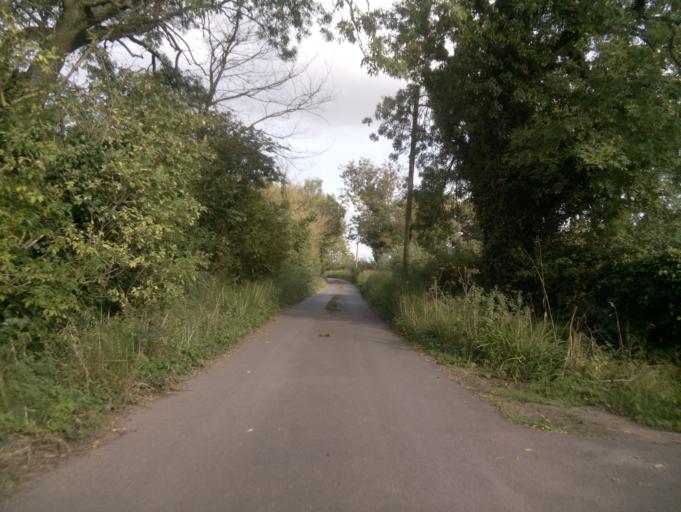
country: GB
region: England
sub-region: South Gloucestershire
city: Alveston
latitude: 51.5683
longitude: -2.5488
